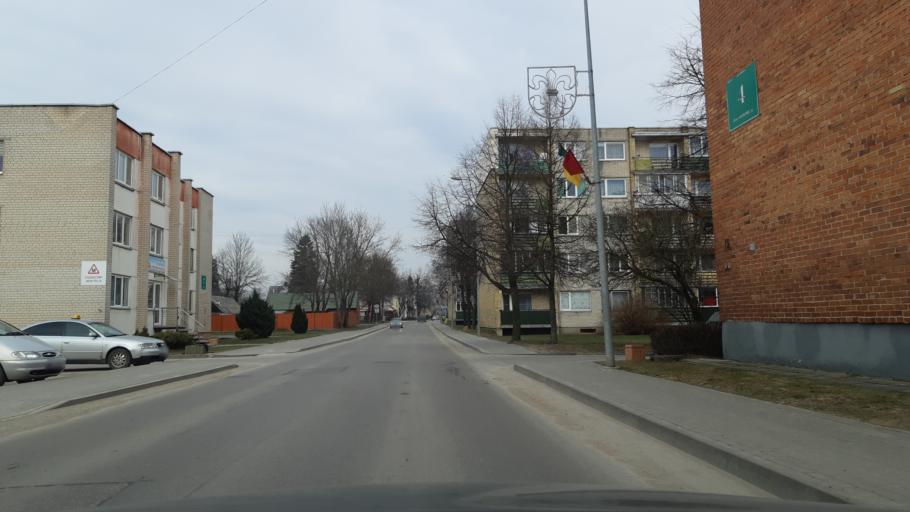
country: LT
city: Vilkaviskis
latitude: 54.6525
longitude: 23.0340
